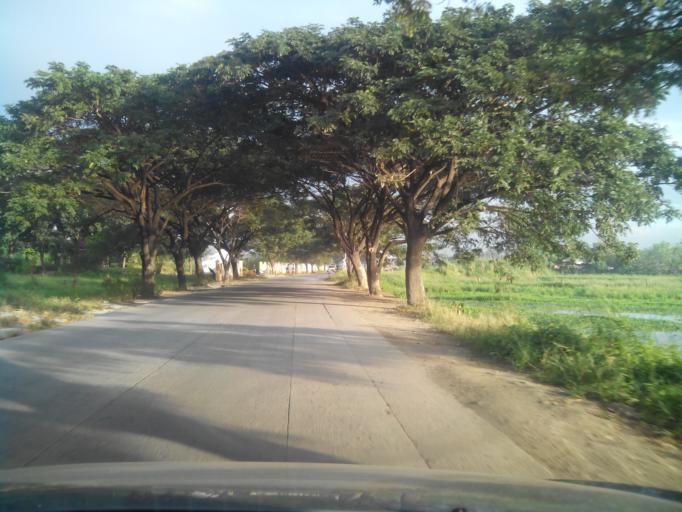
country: PH
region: Calabarzon
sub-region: Province of Rizal
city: Taytay
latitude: 14.5612
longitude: 121.1238
